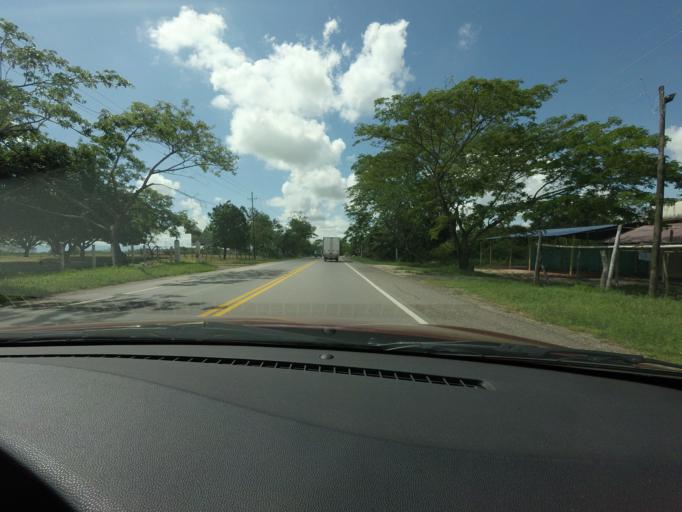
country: CO
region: Tolima
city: Saldana
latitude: 3.9471
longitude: -75.0093
